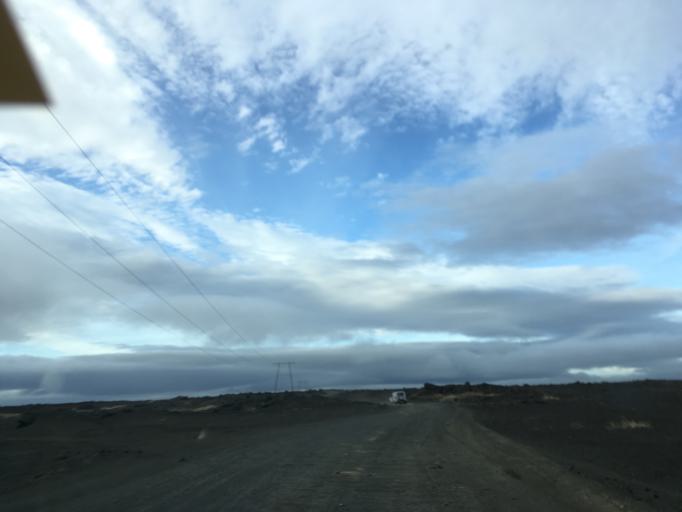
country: IS
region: South
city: Vestmannaeyjar
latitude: 64.1287
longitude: -19.1213
